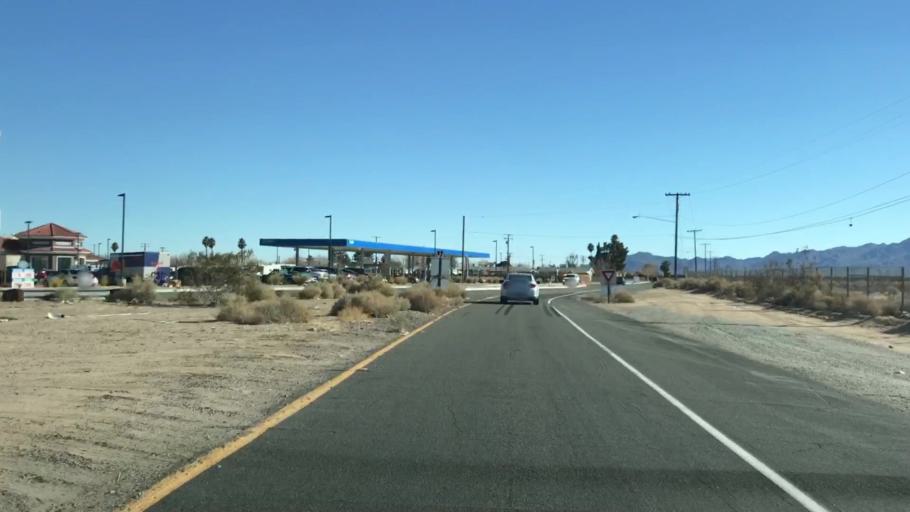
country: US
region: California
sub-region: San Bernardino County
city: Barstow
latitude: 34.9076
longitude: -116.8368
